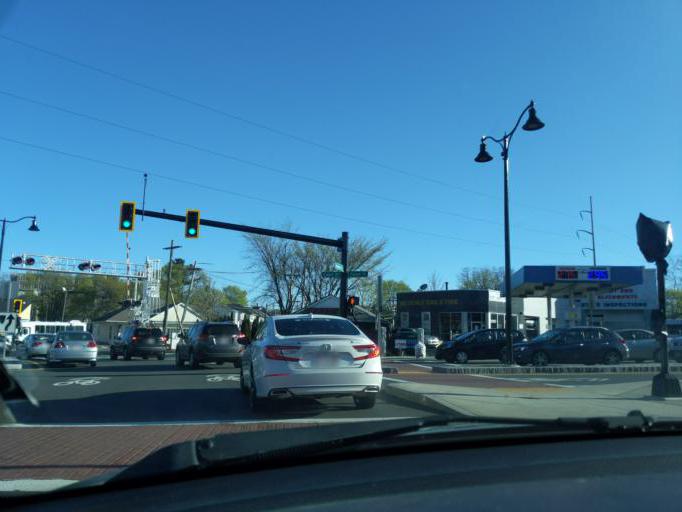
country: US
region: Massachusetts
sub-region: Essex County
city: Beverly
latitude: 42.5574
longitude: -70.8800
